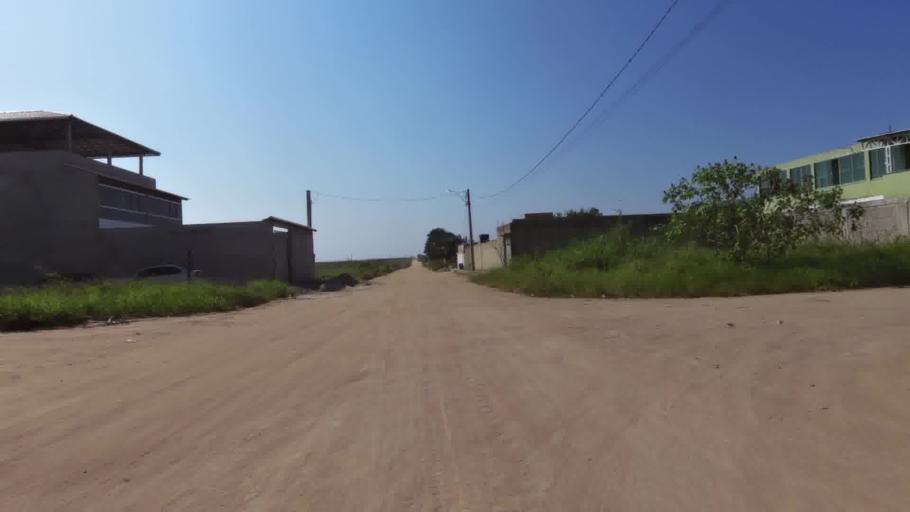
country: BR
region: Espirito Santo
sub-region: Marataizes
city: Marataizes
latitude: -21.0426
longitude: -40.8432
